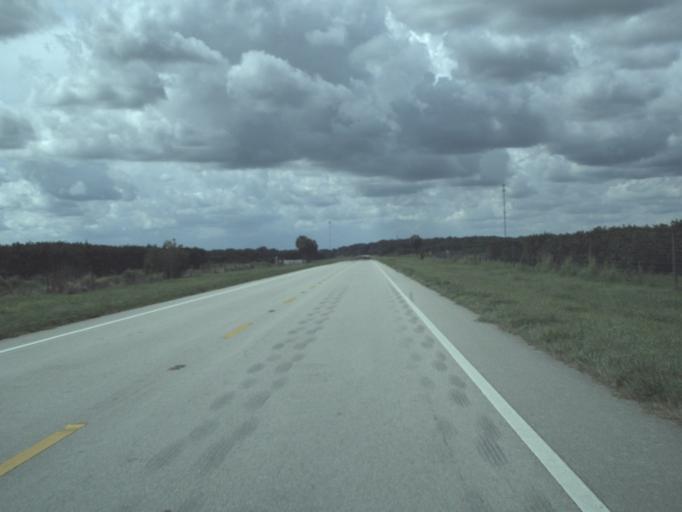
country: US
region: Florida
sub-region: Highlands County
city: Sebring
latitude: 27.4176
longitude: -81.5678
